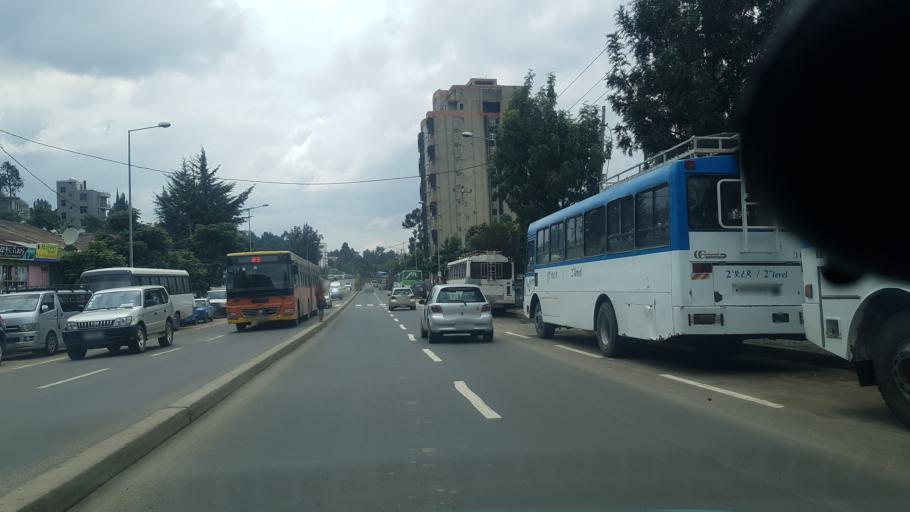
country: ET
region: Adis Abeba
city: Addis Ababa
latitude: 9.0212
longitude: 38.8070
